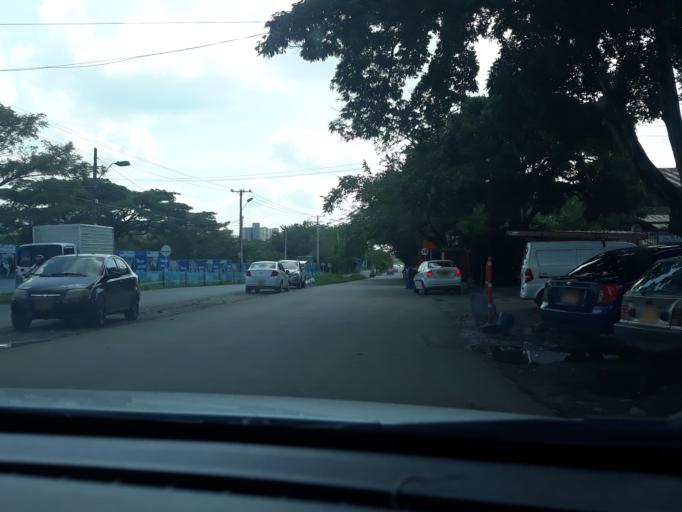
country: CO
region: Valle del Cauca
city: Cali
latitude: 3.3589
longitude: -76.5218
